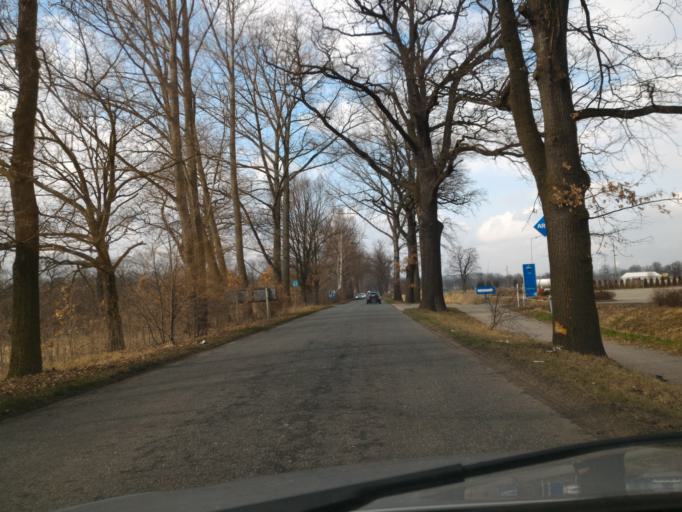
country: DE
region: Saxony
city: Zittau
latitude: 50.8759
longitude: 14.8255
